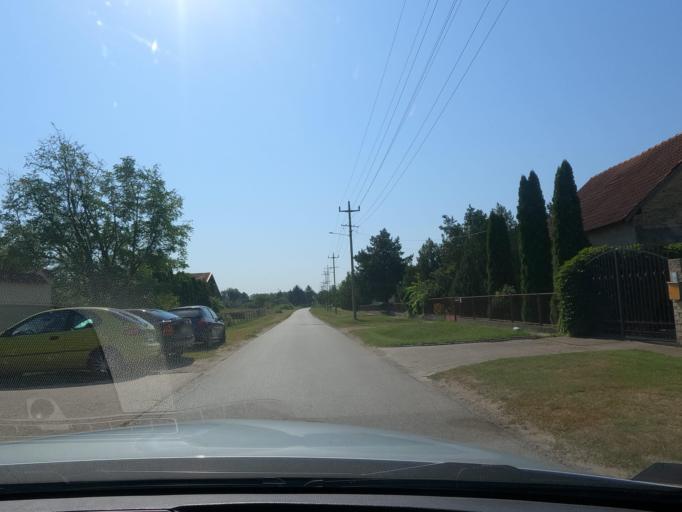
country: HU
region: Csongrad
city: Asotthalom
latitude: 46.1006
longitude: 19.7768
